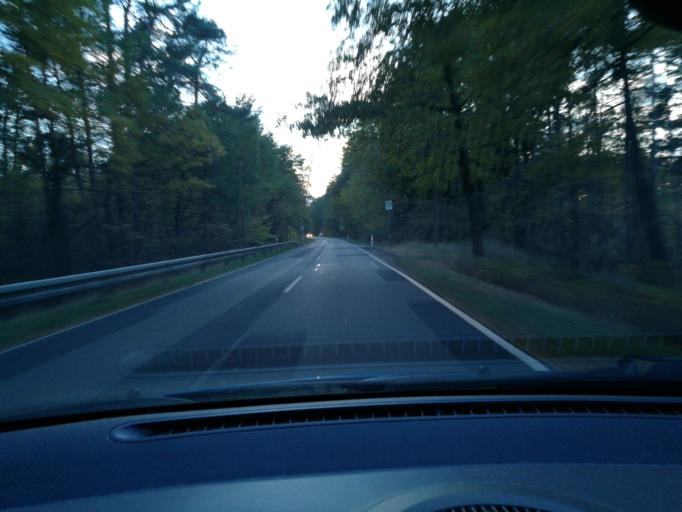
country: DE
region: Brandenburg
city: Lenzen
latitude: 53.0989
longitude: 11.5044
